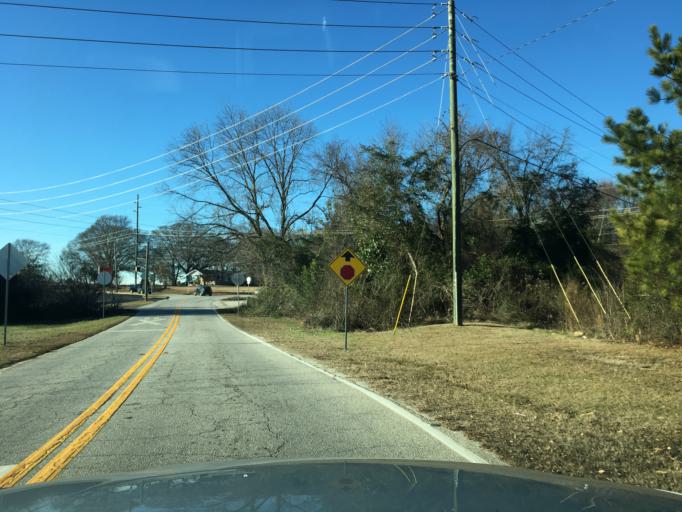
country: US
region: Georgia
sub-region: Rockdale County
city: Conyers
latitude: 33.6735
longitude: -84.0290
